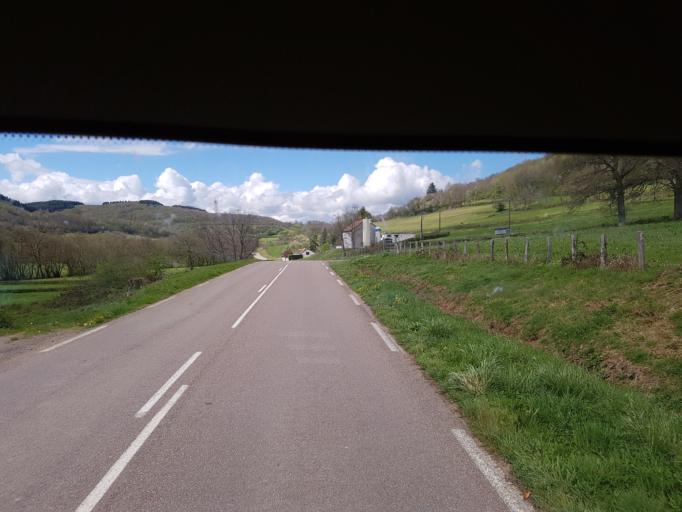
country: FR
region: Bourgogne
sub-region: Departement de Saone-et-Loire
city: Autun
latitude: 47.0933
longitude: 4.2366
